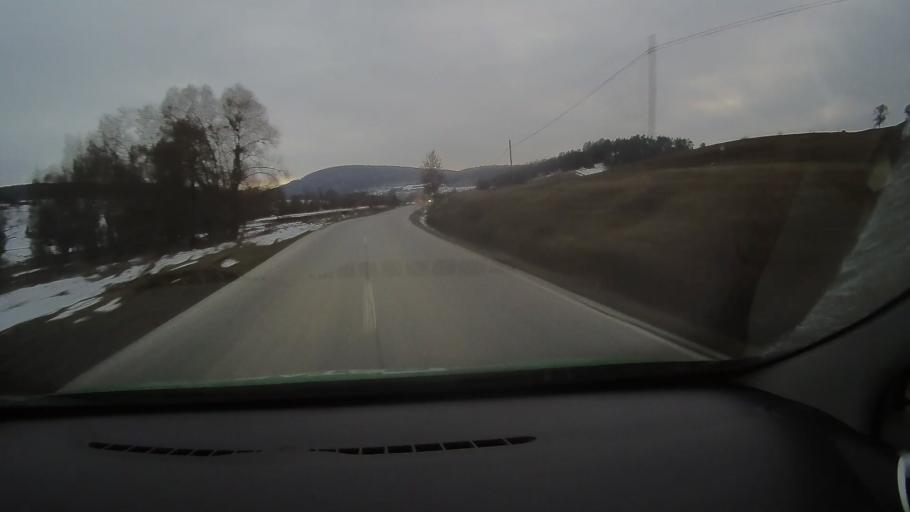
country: RO
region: Harghita
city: Taureni
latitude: 46.2359
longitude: 25.2484
